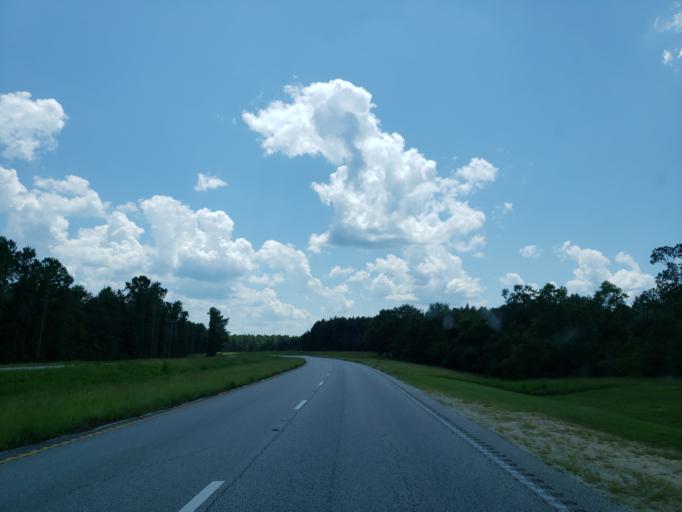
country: US
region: Mississippi
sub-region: Greene County
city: Leakesville
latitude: 31.3518
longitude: -88.5047
